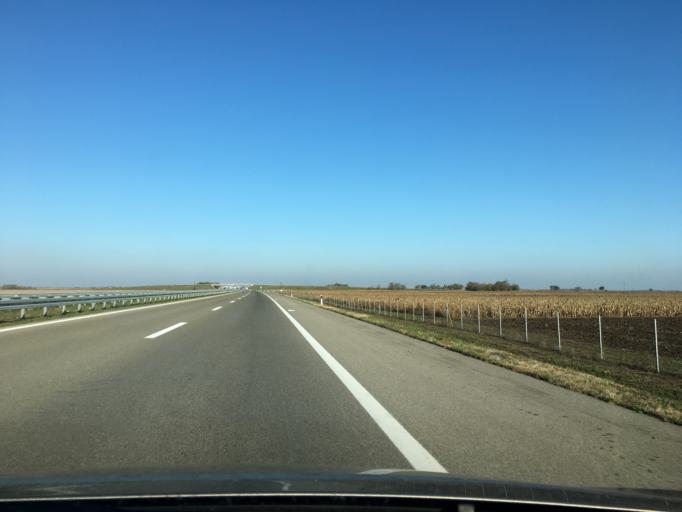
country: RS
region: Autonomna Pokrajina Vojvodina
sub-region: Severnobacki Okrug
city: Backa Topola
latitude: 45.7796
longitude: 19.6991
